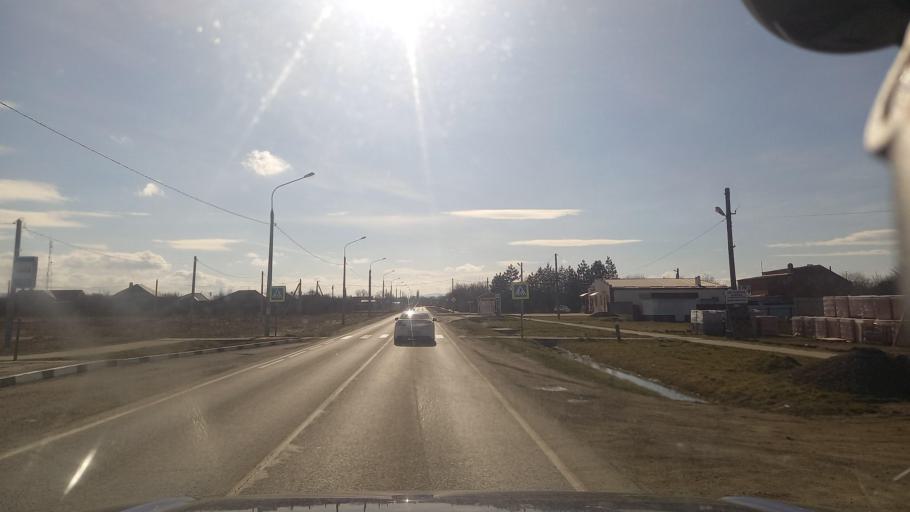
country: RU
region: Krasnodarskiy
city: Novodmitriyevskaya
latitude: 44.8458
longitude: 38.8804
